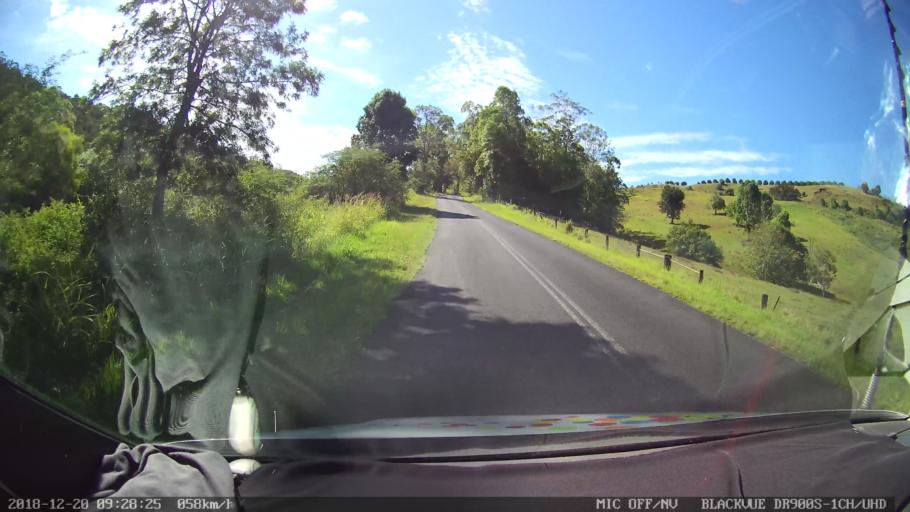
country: AU
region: New South Wales
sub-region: Lismore Municipality
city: Nimbin
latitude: -28.6814
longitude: 153.2846
